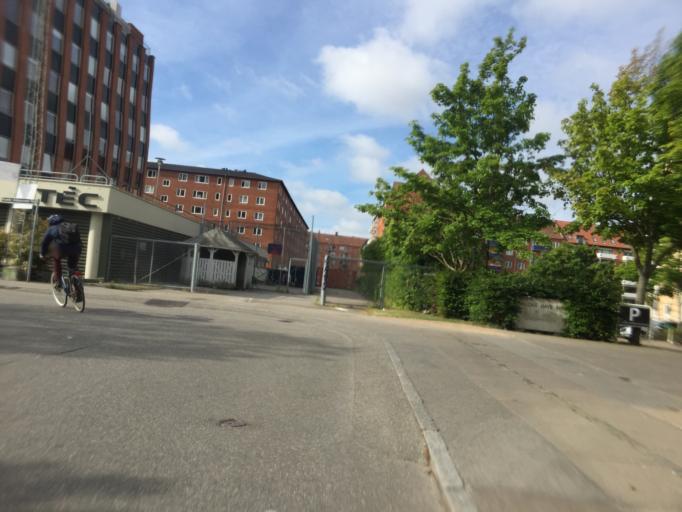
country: DK
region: Capital Region
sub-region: Frederiksberg Kommune
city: Frederiksberg
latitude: 55.6834
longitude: 12.5184
